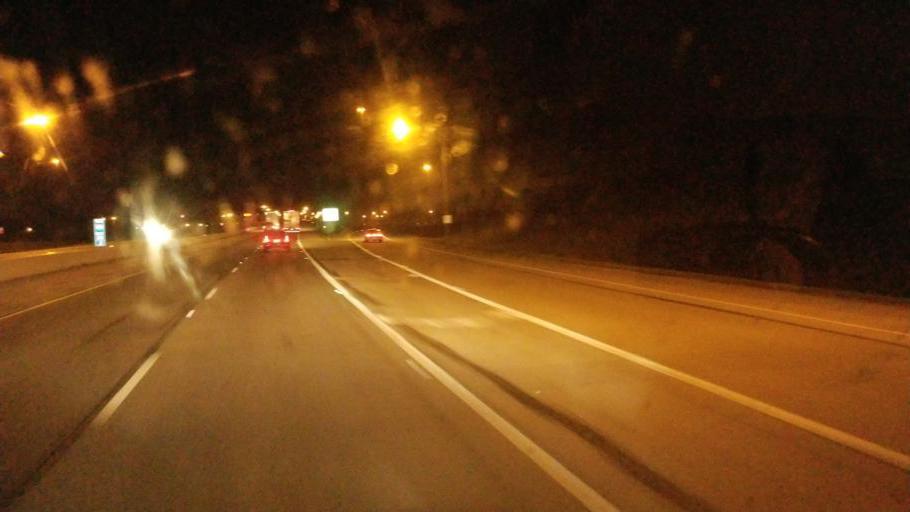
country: US
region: Indiana
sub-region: Allen County
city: Leo-Cedarville
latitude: 41.1579
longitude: -85.0566
